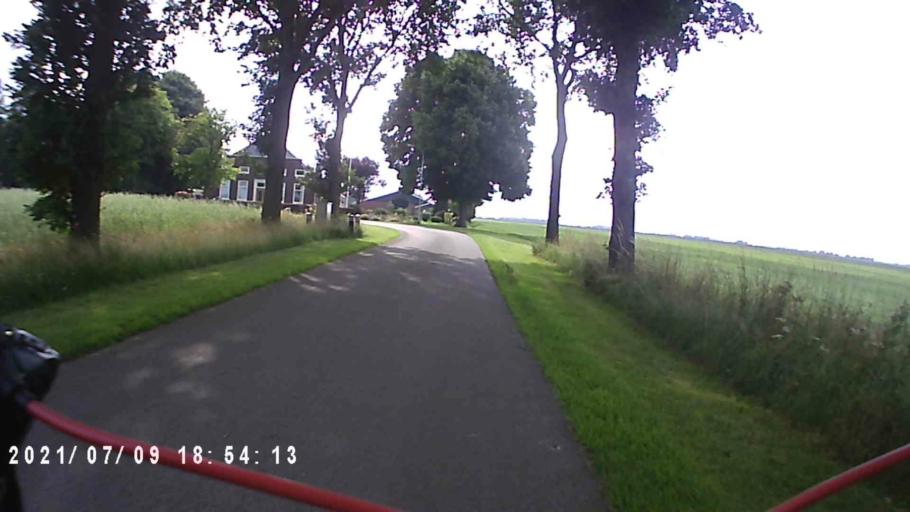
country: NL
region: Groningen
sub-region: Gemeente Stadskanaal
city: Stadskanaal
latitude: 53.0454
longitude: 6.9158
